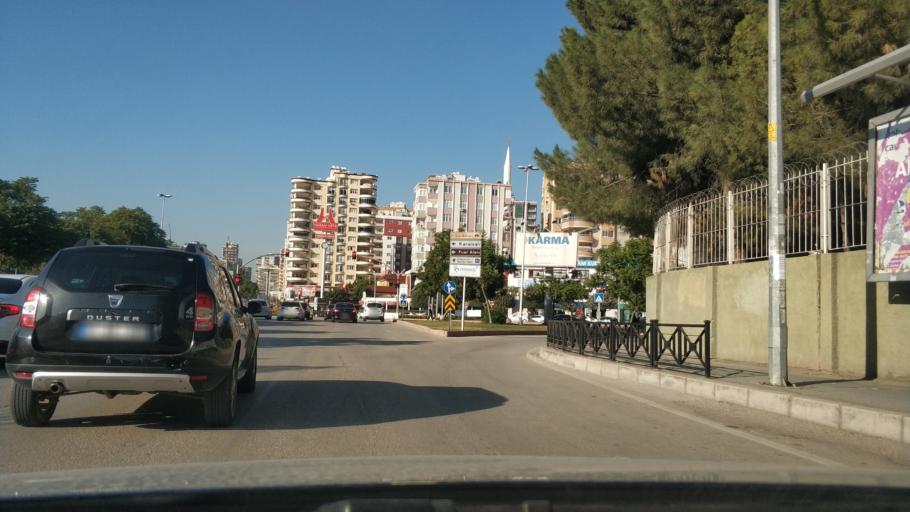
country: TR
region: Adana
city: Seyhan
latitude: 37.0477
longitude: 35.2815
